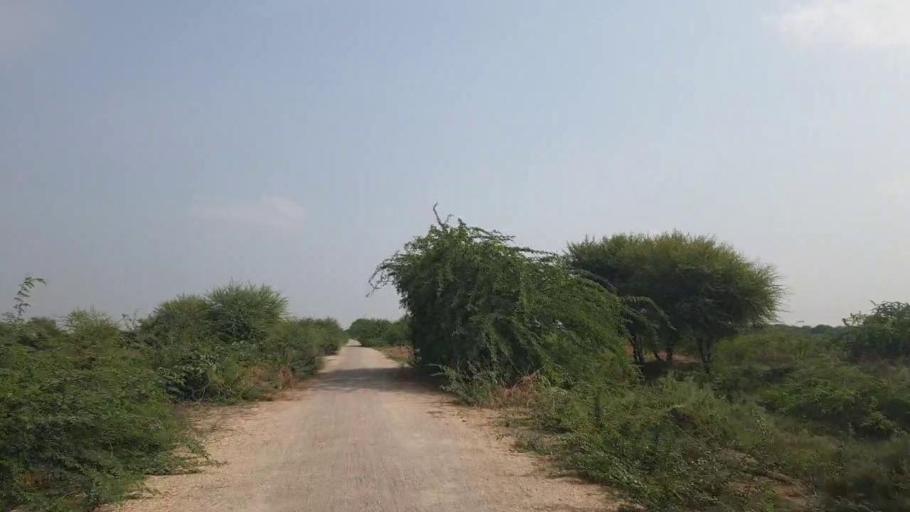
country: PK
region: Sindh
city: Badin
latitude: 24.5474
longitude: 68.6883
